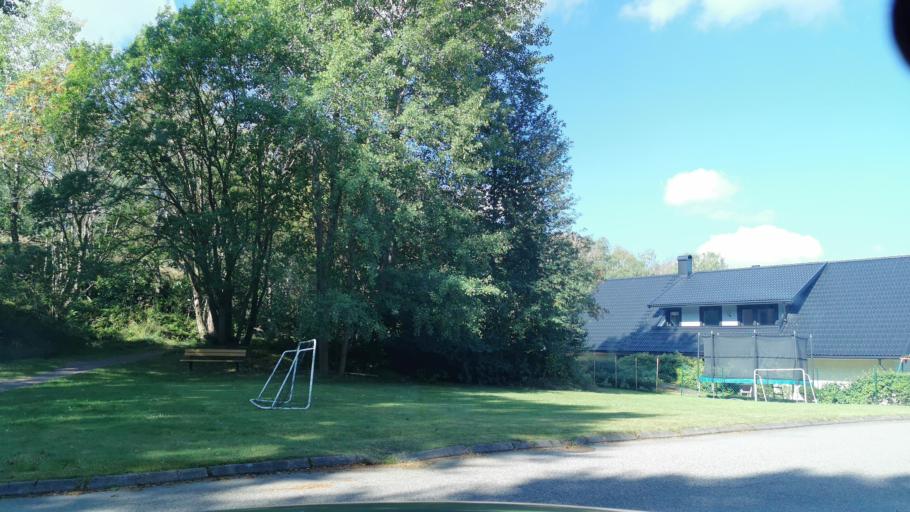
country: SE
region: Vaestra Goetaland
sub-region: Molndal
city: Moelndal
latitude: 57.6728
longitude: 11.9903
